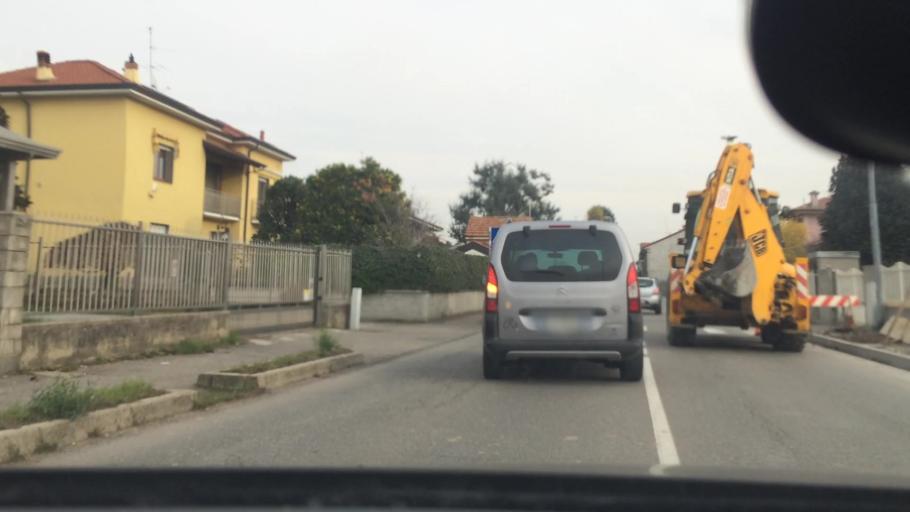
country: IT
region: Lombardy
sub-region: Provincia di Como
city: Rovello Porro
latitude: 45.6524
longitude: 9.0311
